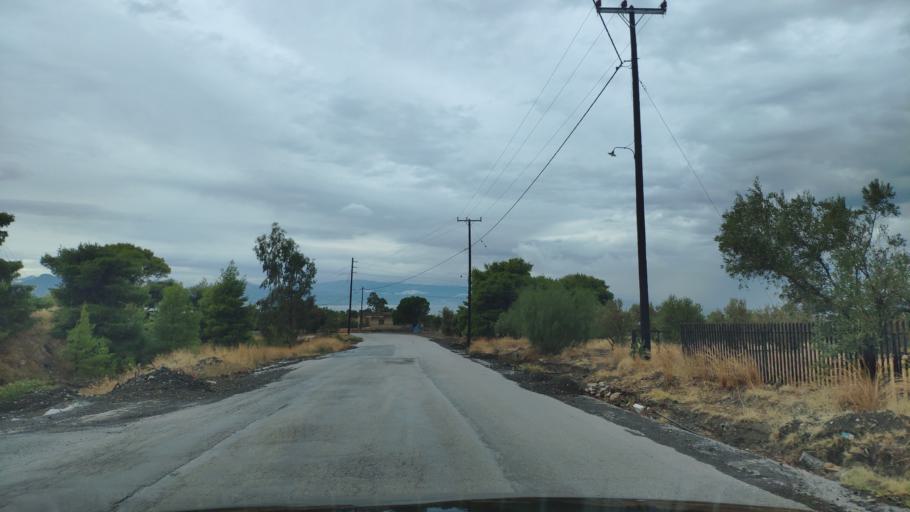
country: GR
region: Peloponnese
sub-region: Nomos Korinthias
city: Loutraki
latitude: 37.9647
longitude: 22.9997
